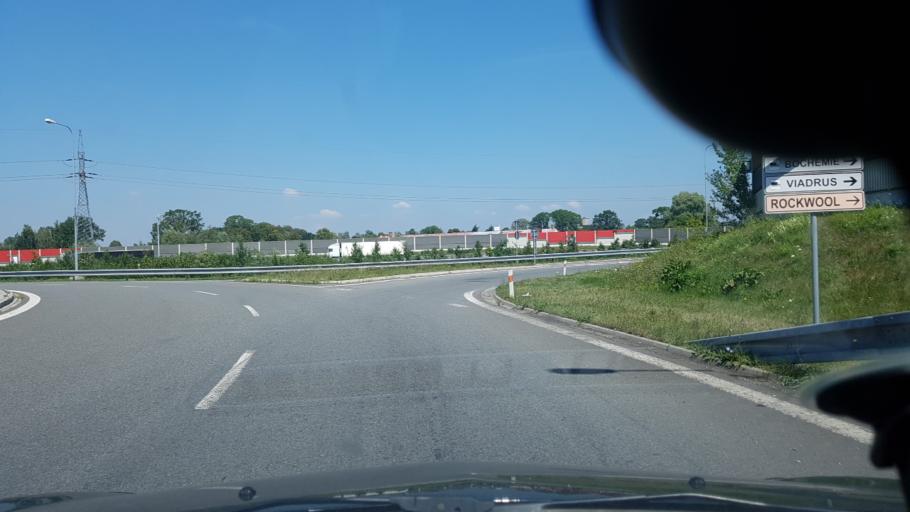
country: CZ
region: Moravskoslezsky
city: Stary Bohumin
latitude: 49.9105
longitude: 18.3356
